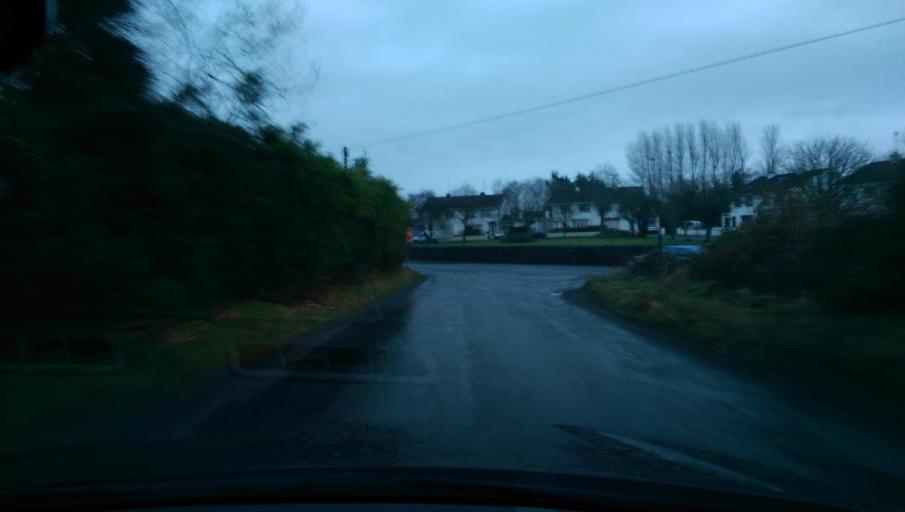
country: IE
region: Connaught
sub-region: County Galway
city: Athenry
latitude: 53.3067
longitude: -8.7417
